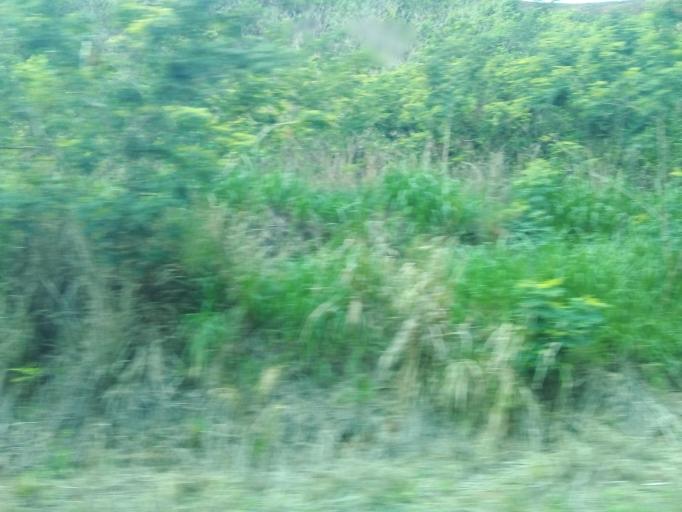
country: BR
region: Minas Gerais
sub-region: Governador Valadares
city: Governador Valadares
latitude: -18.9245
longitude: -42.0225
